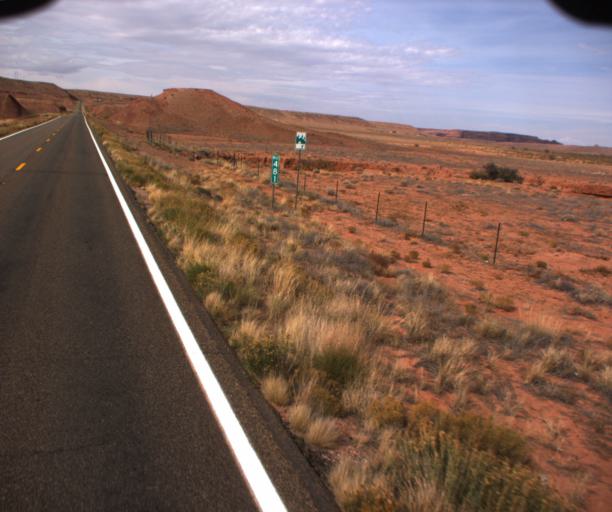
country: US
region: Arizona
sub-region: Apache County
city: Many Farms
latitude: 36.5364
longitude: -109.5161
